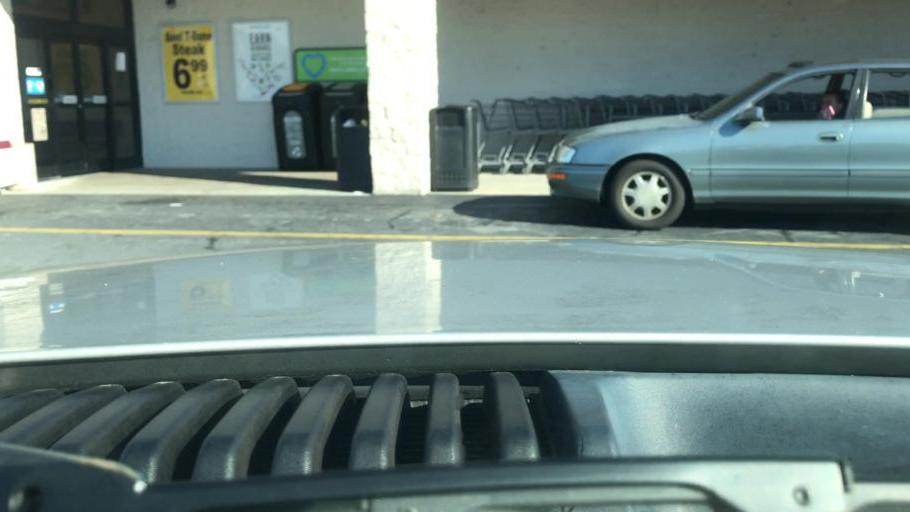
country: US
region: North Carolina
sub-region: Yadkin County
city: Jonesville
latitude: 36.2389
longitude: -80.8319
